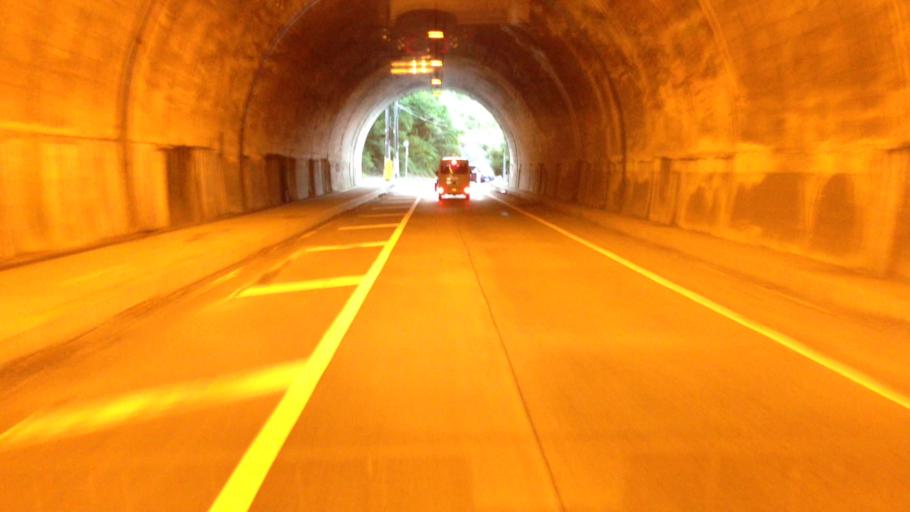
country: JP
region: Kanagawa
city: Yokosuka
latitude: 35.2343
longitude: 139.6581
